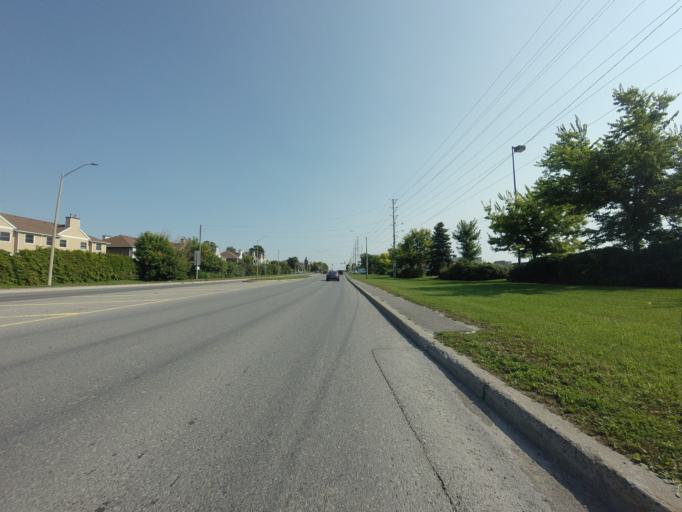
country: CA
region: Ontario
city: Bells Corners
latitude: 45.2679
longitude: -75.7529
